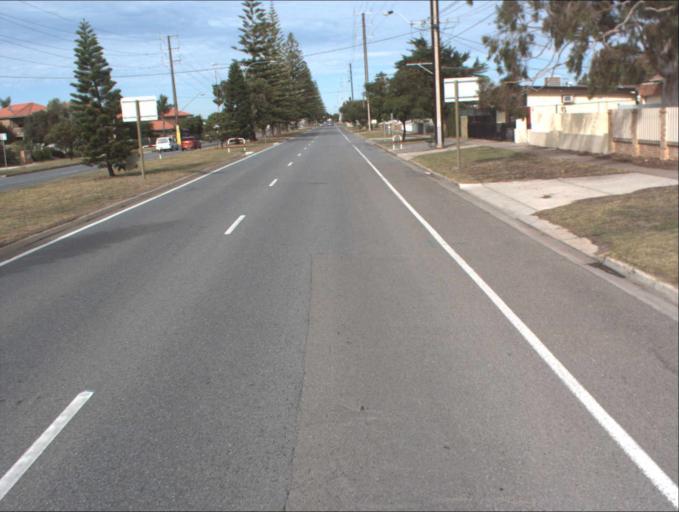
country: AU
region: South Australia
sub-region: Port Adelaide Enfield
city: Birkenhead
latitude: -34.8134
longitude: 138.5012
